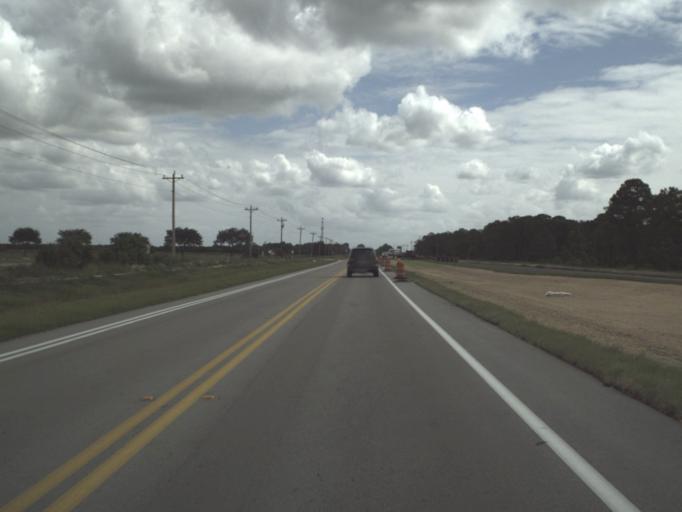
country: US
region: Florida
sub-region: Lee County
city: Lehigh Acres
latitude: 26.5159
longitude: -81.5533
